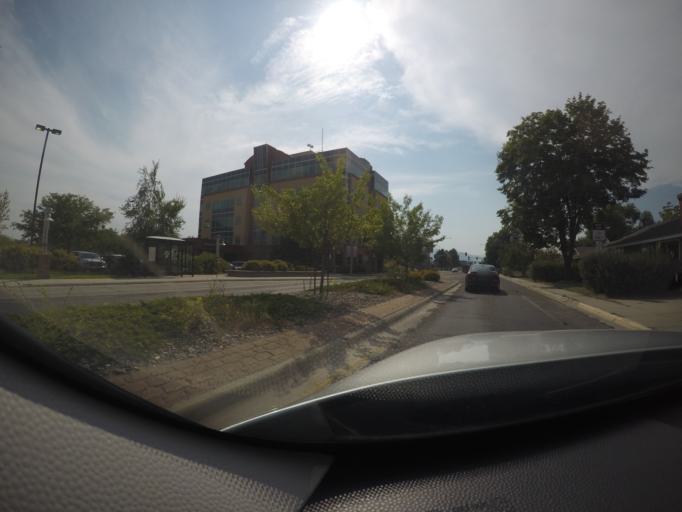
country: US
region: Montana
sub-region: Missoula County
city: Orchard Homes
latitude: 46.8489
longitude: -114.0246
